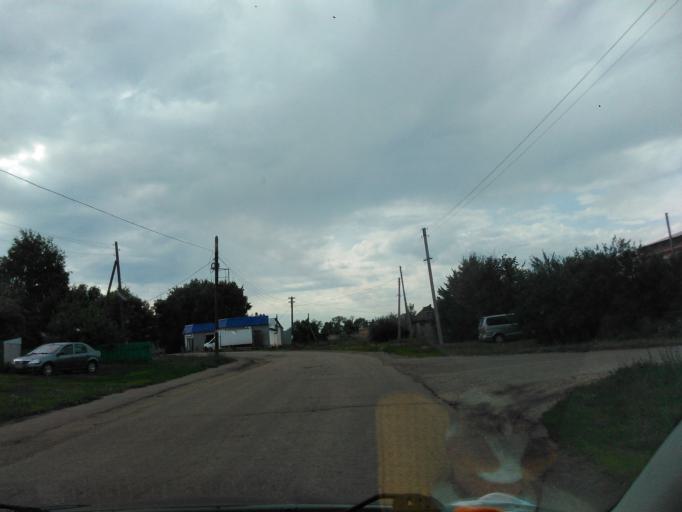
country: RU
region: Penza
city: Poim
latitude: 53.0307
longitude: 43.1762
